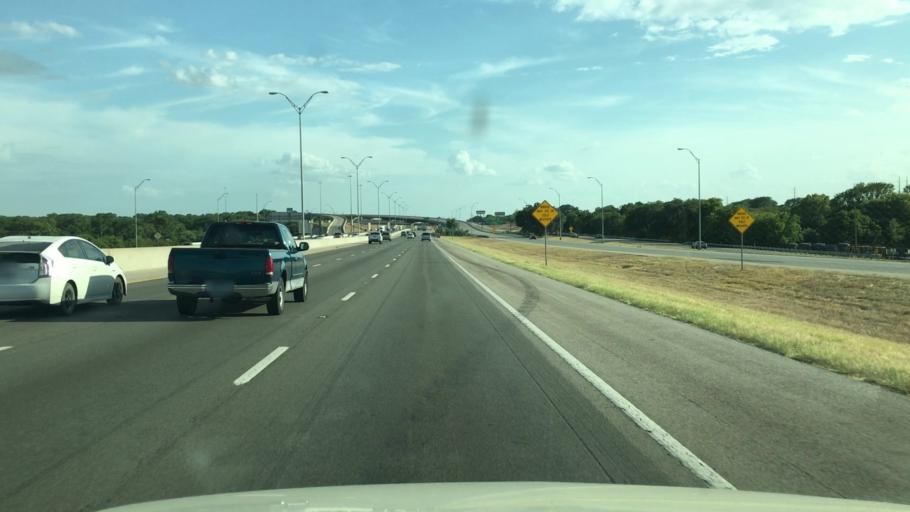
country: US
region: Texas
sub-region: Williamson County
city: Serenada
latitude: 30.6954
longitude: -97.6545
